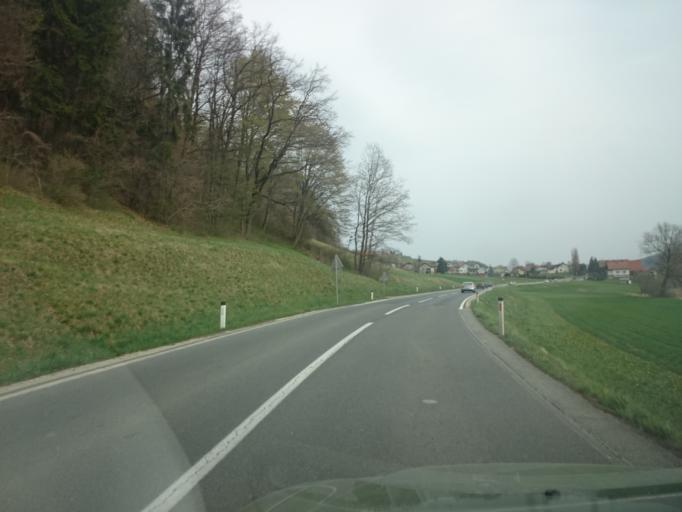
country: SI
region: Store
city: Store
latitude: 46.2207
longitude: 15.3449
